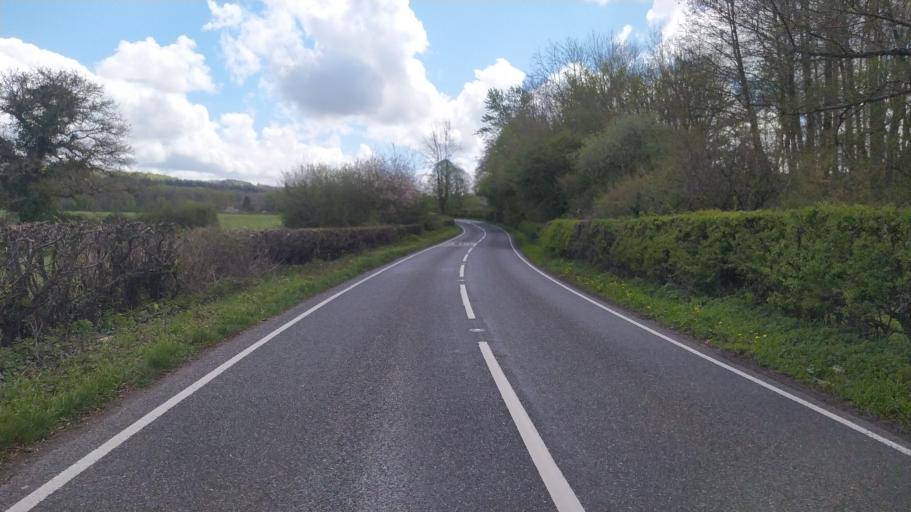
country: GB
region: England
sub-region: Somerset
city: Frome
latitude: 51.1785
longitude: -2.3085
